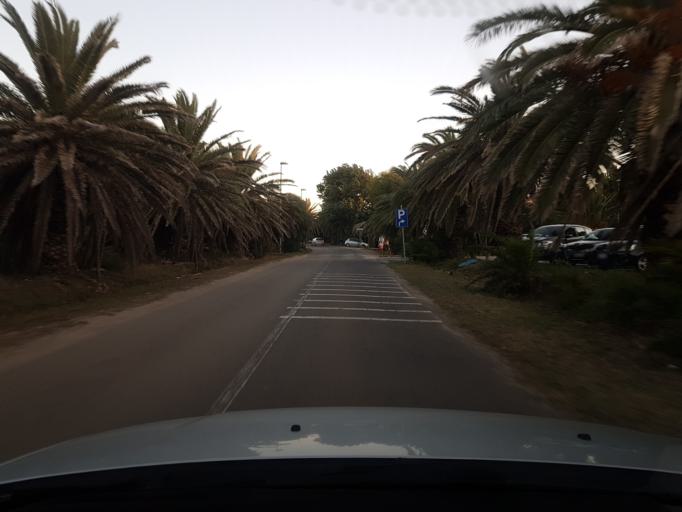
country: IT
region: Sardinia
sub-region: Provincia di Oristano
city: Riola Sardo
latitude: 40.0351
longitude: 8.3996
